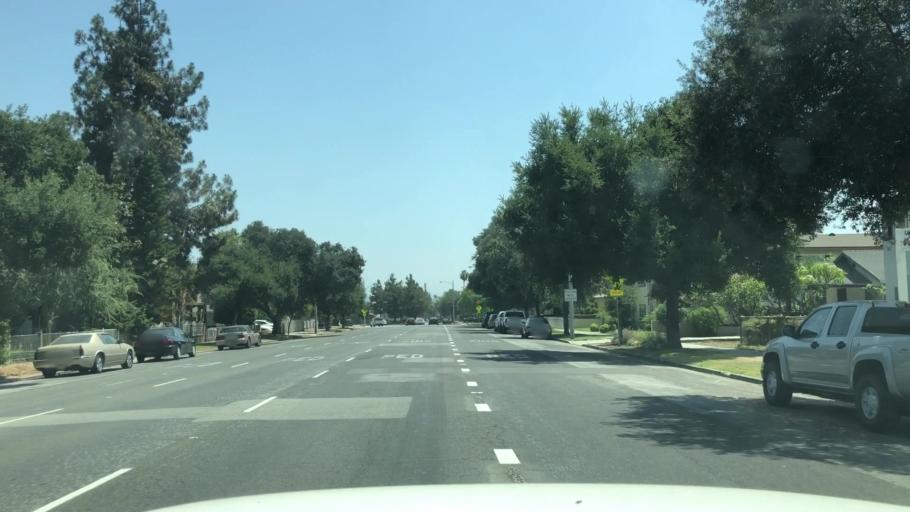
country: US
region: California
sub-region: Los Angeles County
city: Azusa
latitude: 34.1257
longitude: -117.9089
